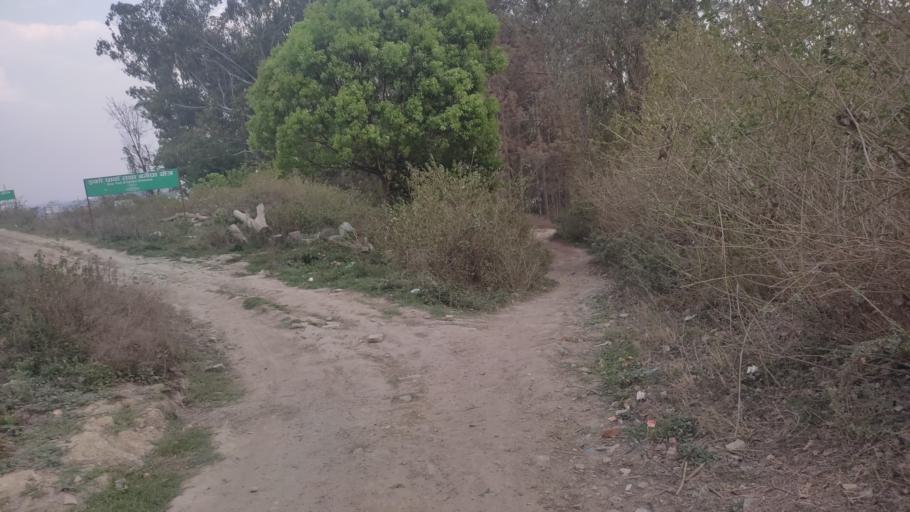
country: NP
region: Central Region
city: Kirtipur
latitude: 27.6813
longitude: 85.2879
